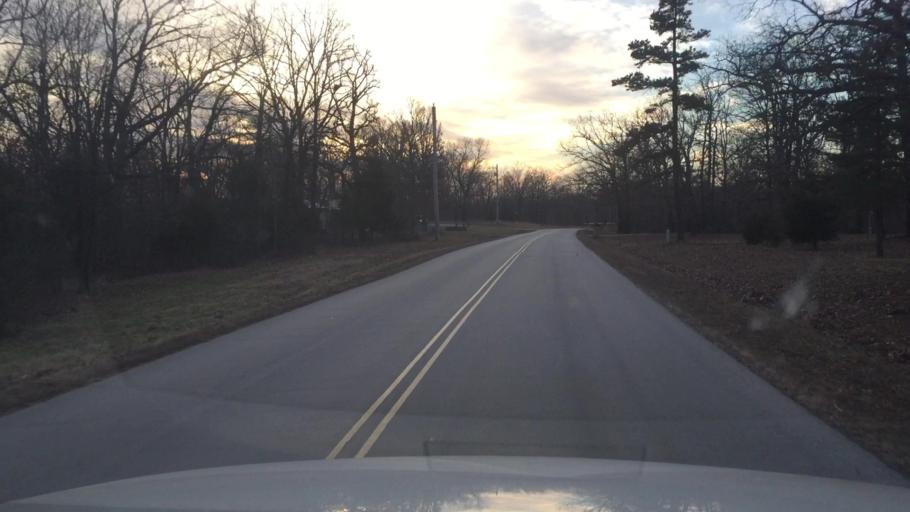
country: US
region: Missouri
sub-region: Morgan County
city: Versailles
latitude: 38.3362
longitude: -92.7621
